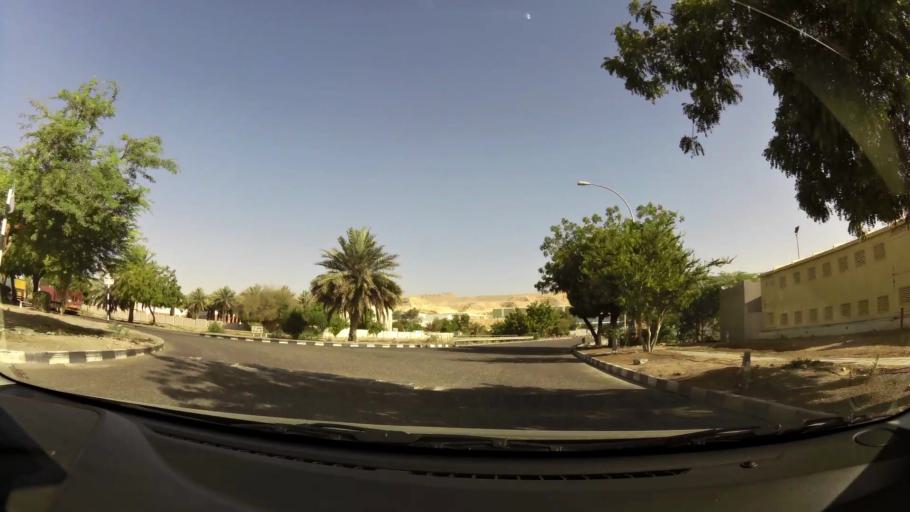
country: OM
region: Muhafazat Masqat
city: As Sib al Jadidah
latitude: 23.5557
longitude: 58.2140
